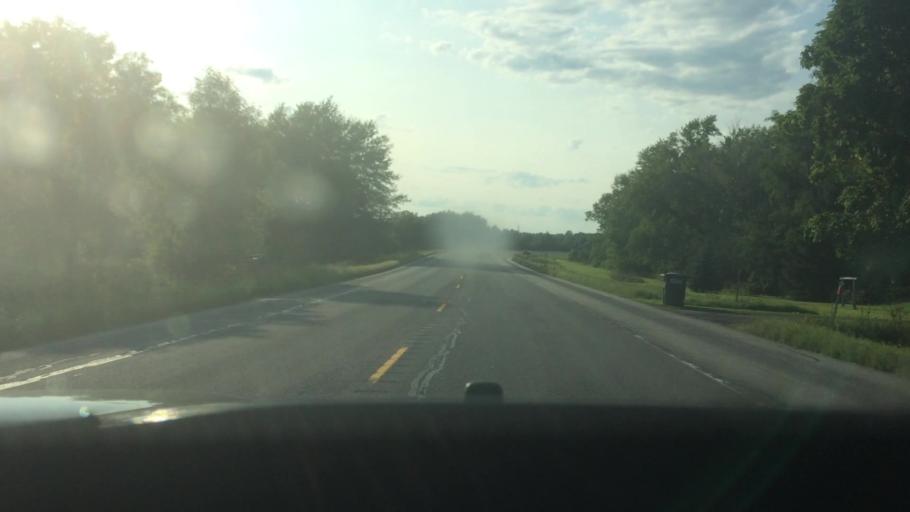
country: US
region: New York
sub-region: St. Lawrence County
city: Canton
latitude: 44.6071
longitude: -75.2086
